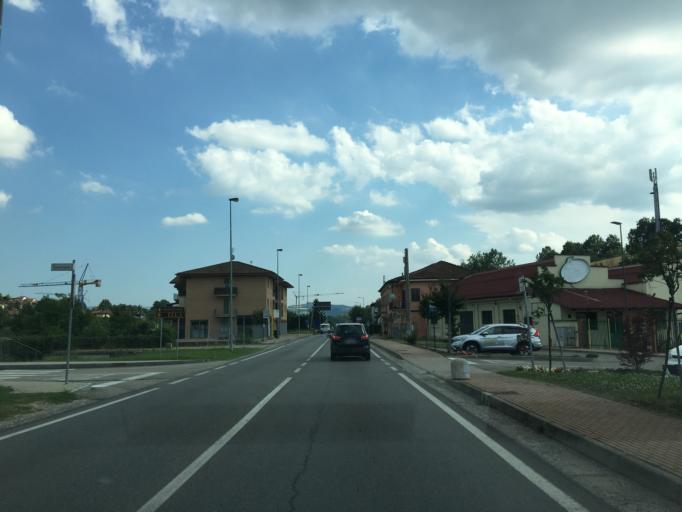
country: IT
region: Piedmont
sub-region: Provincia di Cuneo
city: Mussotto
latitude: 44.7276
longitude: 8.0082
